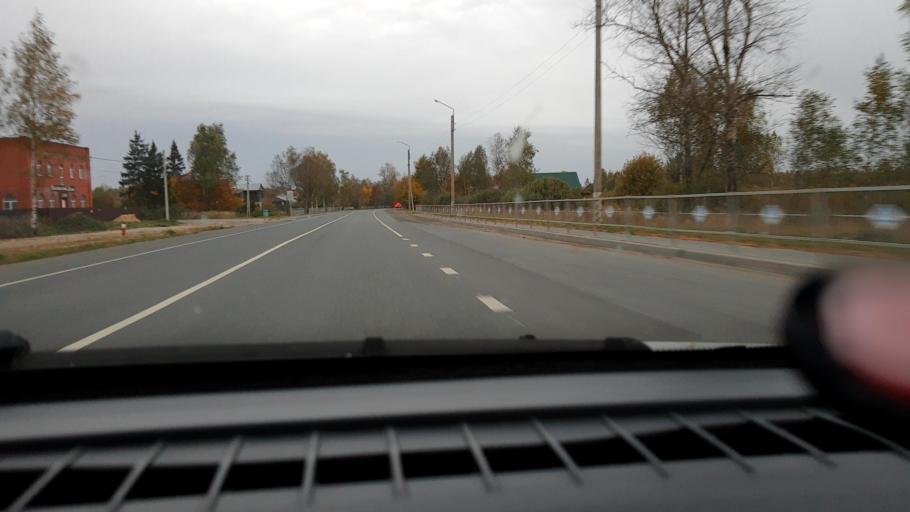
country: RU
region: Vladimir
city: Orgtrud
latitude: 56.2079
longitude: 40.6781
